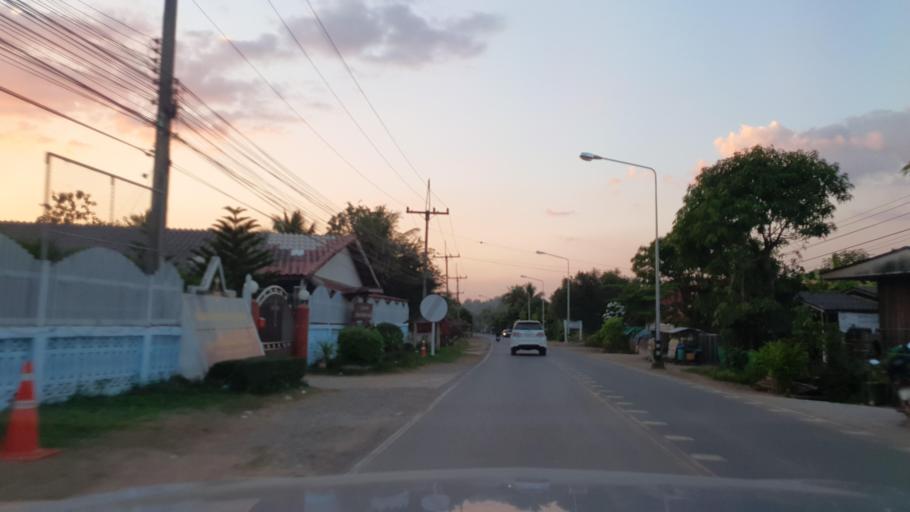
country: TH
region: Phayao
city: Dok Kham Tai
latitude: 19.0430
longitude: 100.0621
